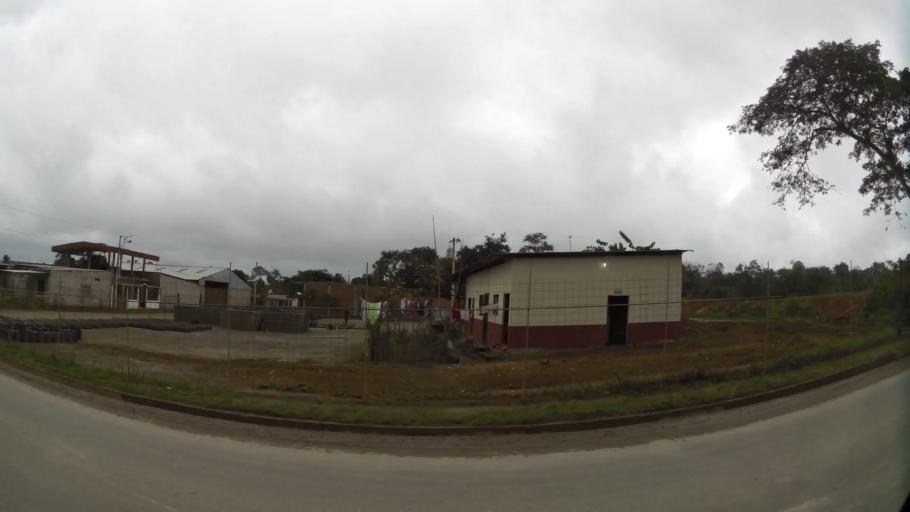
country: EC
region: El Oro
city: Pasaje
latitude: -3.3290
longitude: -79.7664
